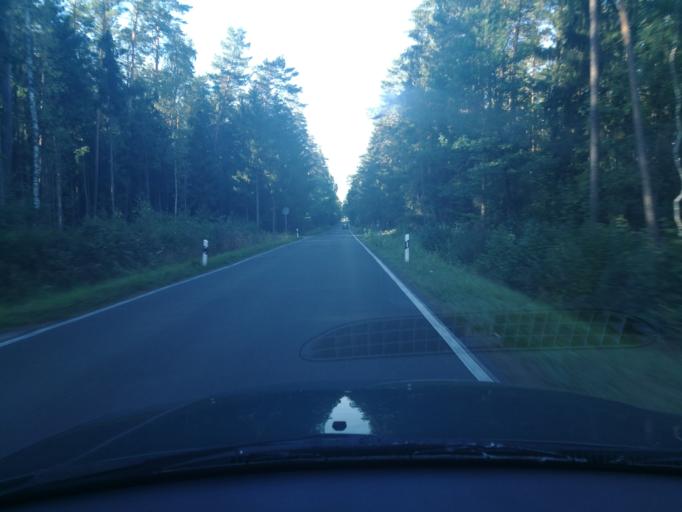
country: DE
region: Bavaria
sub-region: Regierungsbezirk Mittelfranken
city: Hessdorf
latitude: 49.6176
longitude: 10.9384
